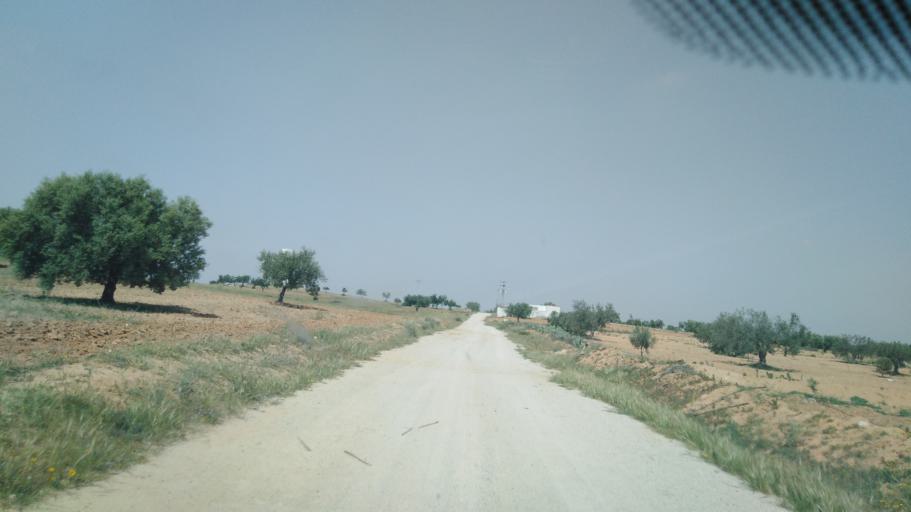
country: TN
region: Safaqis
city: Sfax
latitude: 34.7506
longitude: 10.5654
